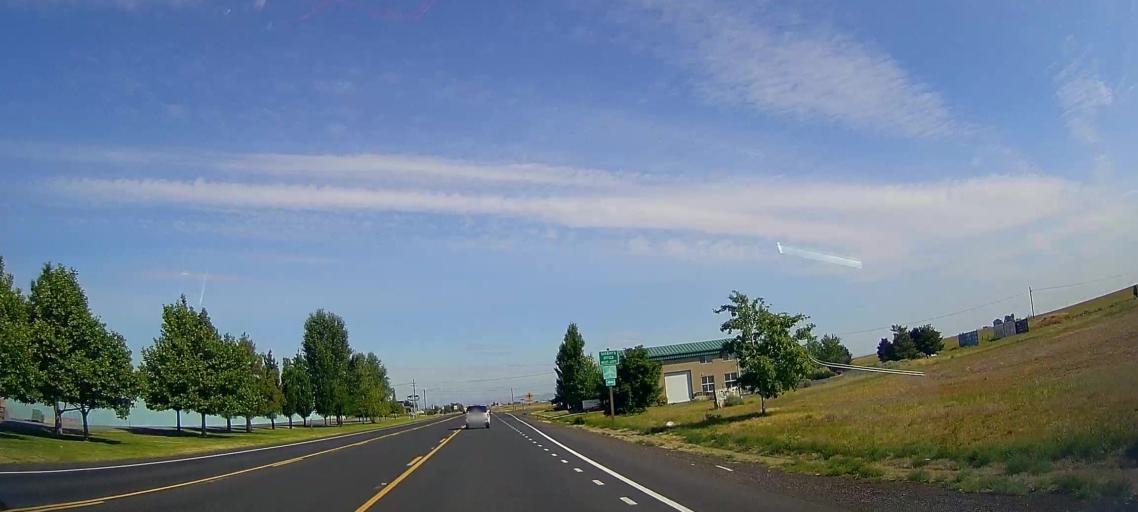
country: US
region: Oregon
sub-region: Jefferson County
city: Madras
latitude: 44.6630
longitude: -121.1347
